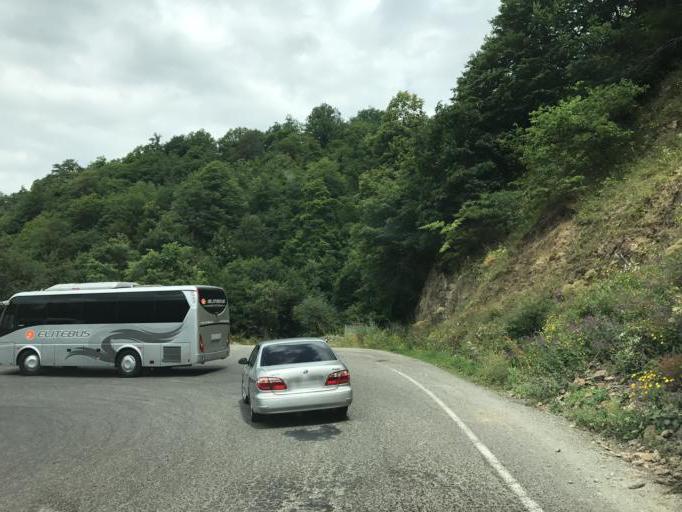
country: AM
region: Tavush
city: Dilijan
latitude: 40.6930
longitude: 44.8599
